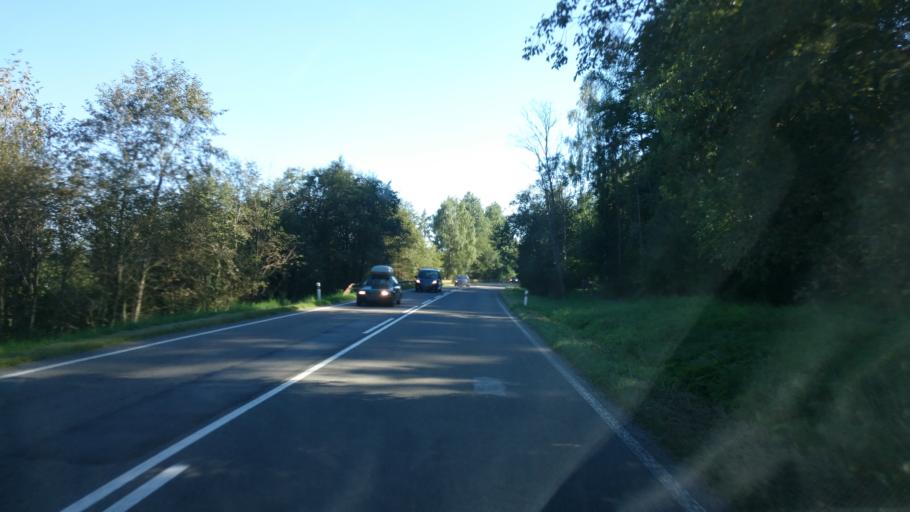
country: SK
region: Presovsky
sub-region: Okres Poprad
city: Vysoke Tatry
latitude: 49.1614
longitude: 20.2719
